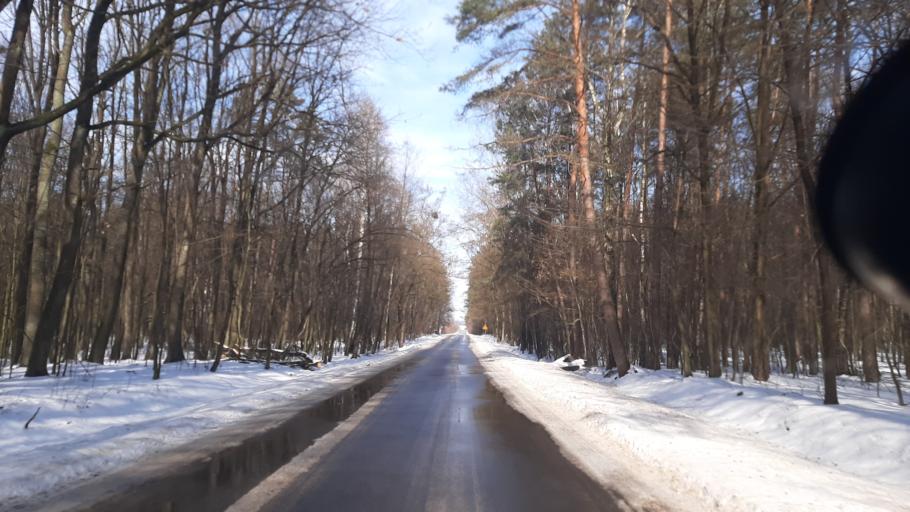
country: PL
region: Lublin Voivodeship
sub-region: Powiat pulawski
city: Kurow
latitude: 51.4374
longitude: 22.1931
